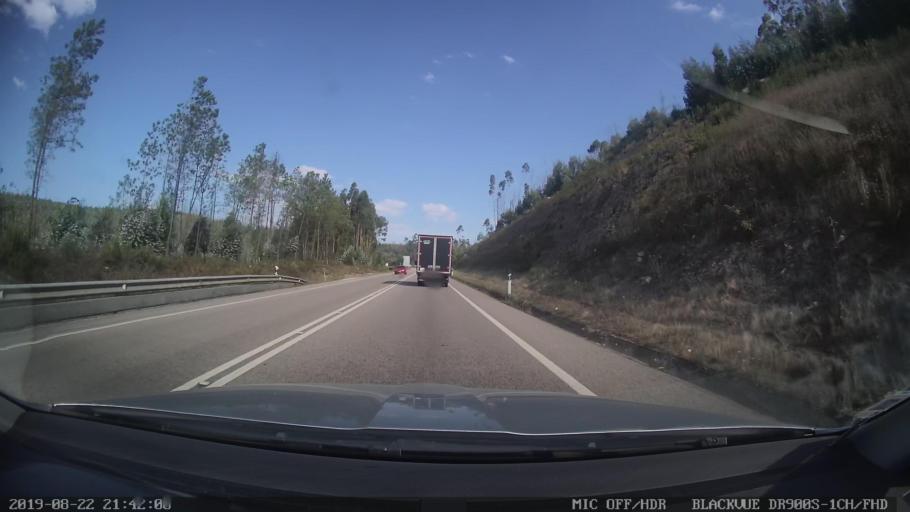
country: PT
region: Leiria
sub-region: Figueiro Dos Vinhos
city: Figueiro dos Vinhos
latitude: 39.9291
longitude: -8.3345
